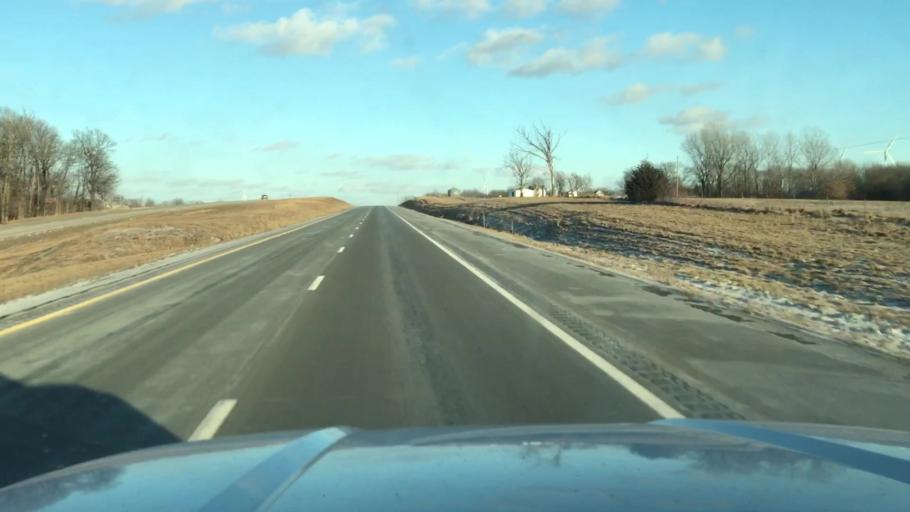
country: US
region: Missouri
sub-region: DeKalb County
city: Maysville
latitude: 39.7620
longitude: -94.4677
